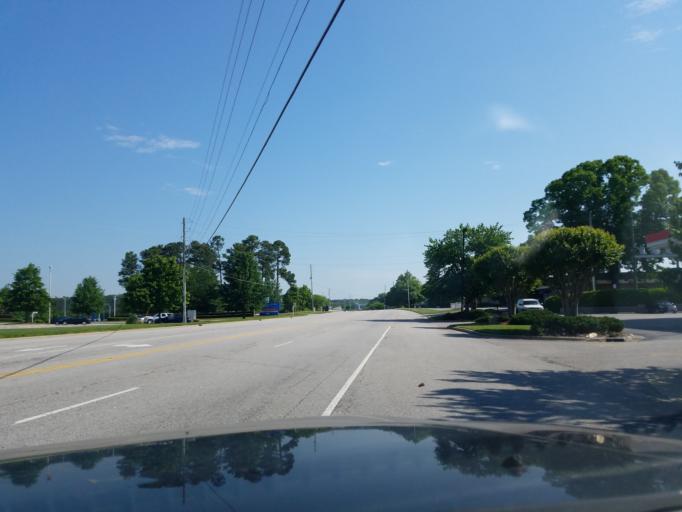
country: US
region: North Carolina
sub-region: Vance County
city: South Henderson
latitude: 36.3302
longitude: -78.4479
